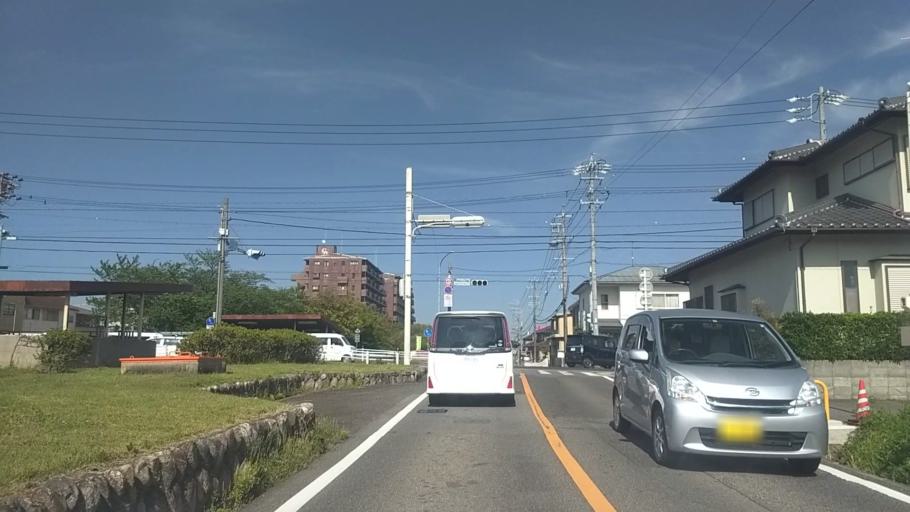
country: JP
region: Aichi
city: Anjo
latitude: 34.9766
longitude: 137.0842
